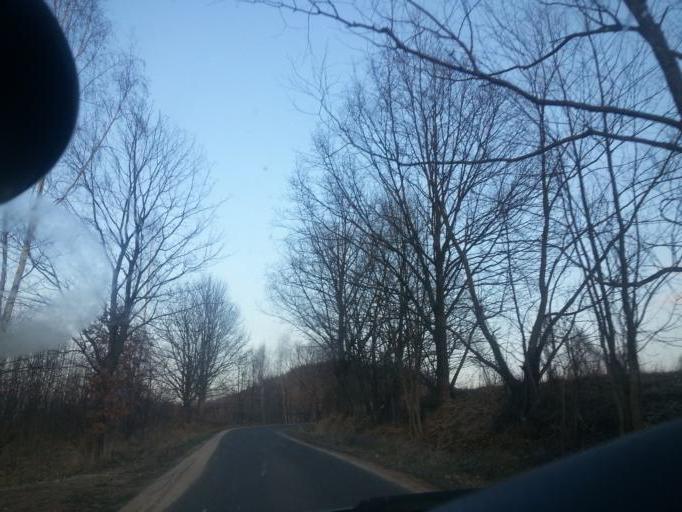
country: PL
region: Lower Silesian Voivodeship
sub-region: Powiat lwowecki
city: Wlen
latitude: 50.9734
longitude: 15.6358
